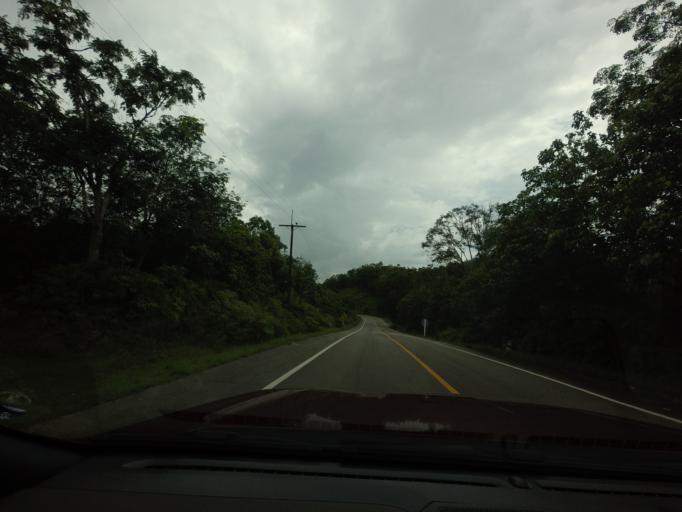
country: TH
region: Narathiwat
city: Sukhirin
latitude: 5.9797
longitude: 101.7009
